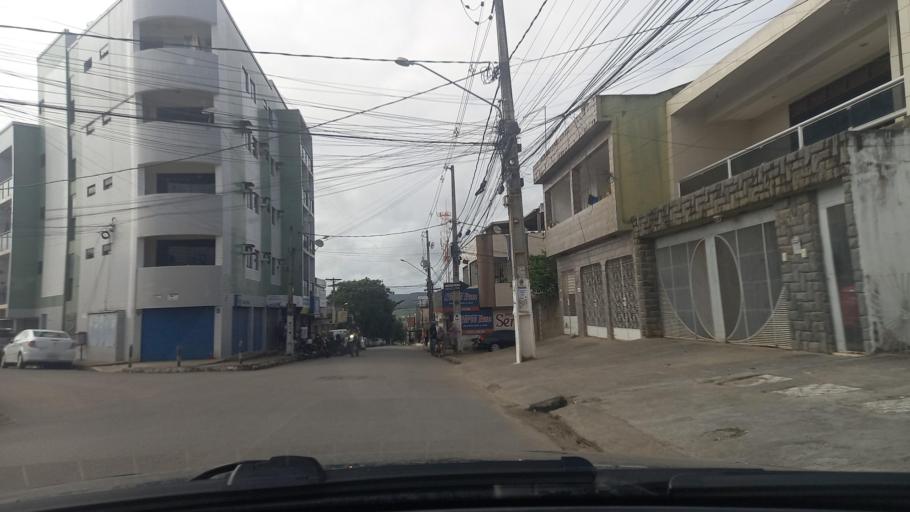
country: BR
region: Pernambuco
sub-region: Vitoria De Santo Antao
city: Vitoria de Santo Antao
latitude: -8.1080
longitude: -35.3003
